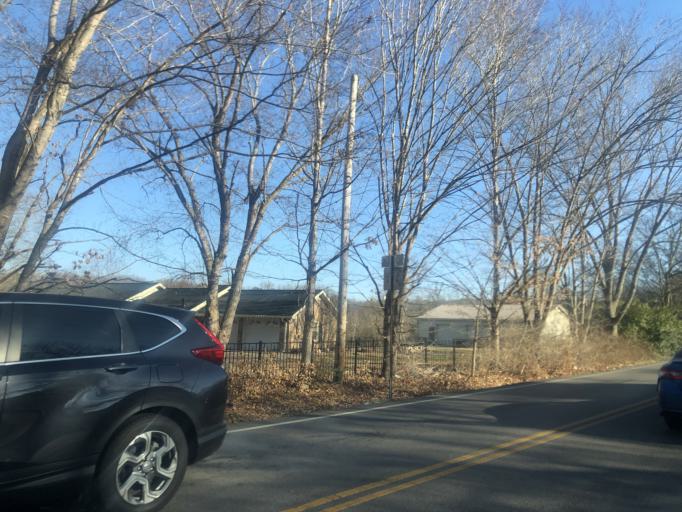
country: US
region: Tennessee
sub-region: Williamson County
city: Nolensville
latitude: 36.0253
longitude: -86.6647
